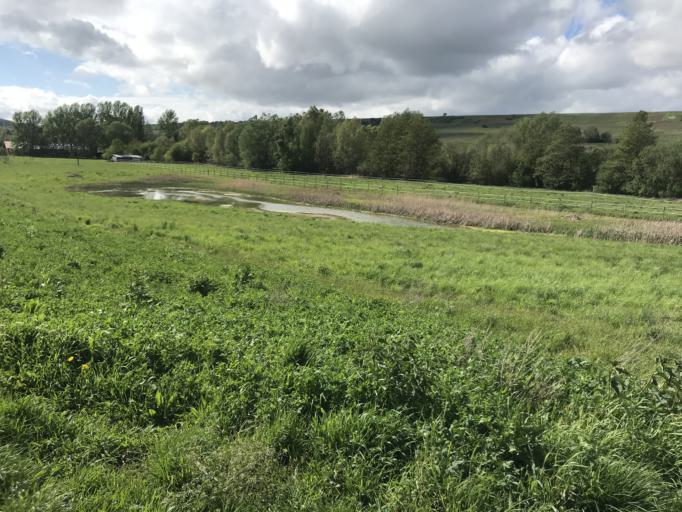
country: DE
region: Rheinland-Pfalz
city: Jugenheim
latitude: 49.8932
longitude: 8.1000
